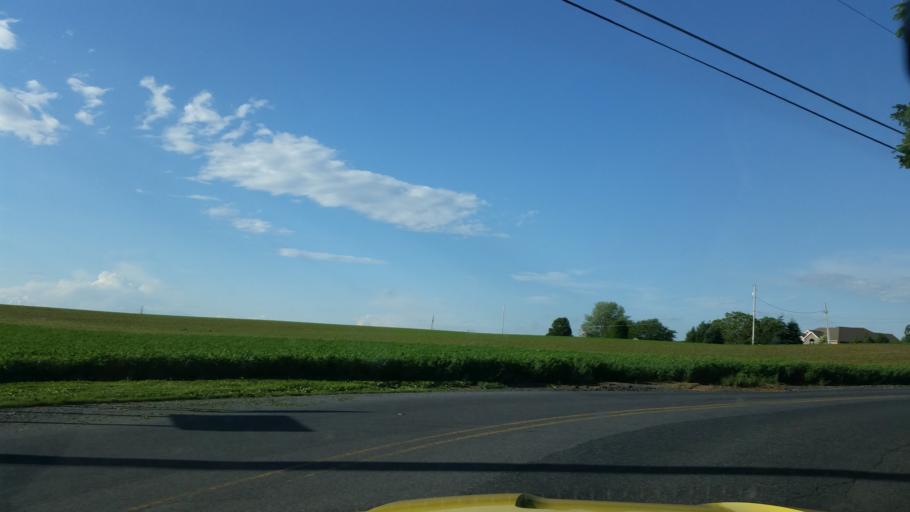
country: US
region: Pennsylvania
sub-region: Lebanon County
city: Avon
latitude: 40.3272
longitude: -76.3628
